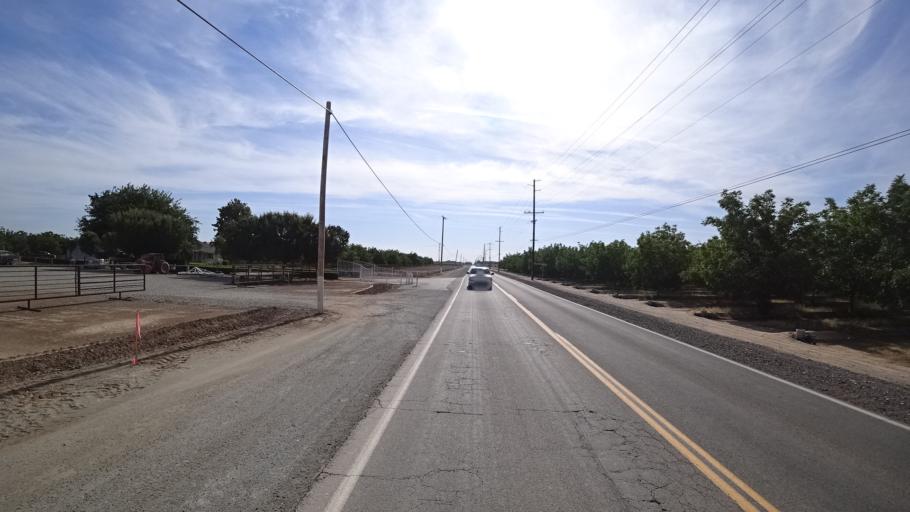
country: US
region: California
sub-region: Kings County
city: Hanford
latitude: 36.3426
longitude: -119.5962
